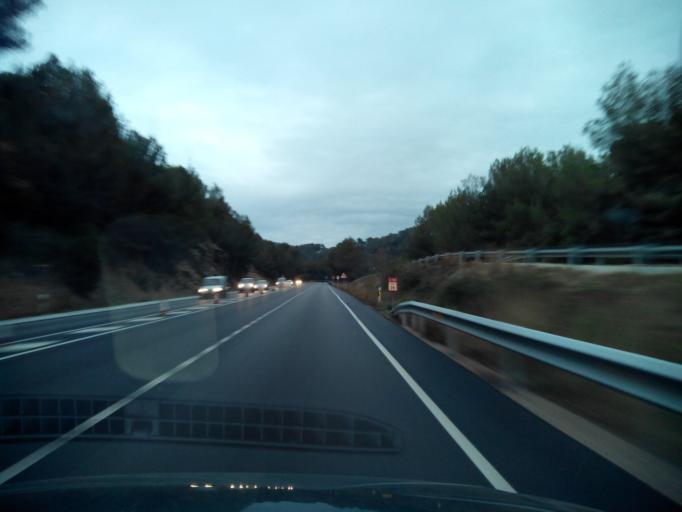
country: ES
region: Catalonia
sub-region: Provincia de Barcelona
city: Viladecavalls
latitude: 41.5704
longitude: 1.9629
